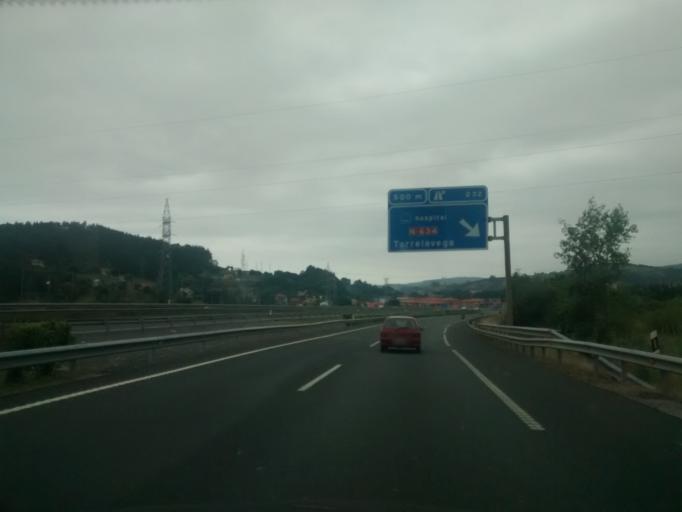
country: ES
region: Cantabria
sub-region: Provincia de Cantabria
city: Reocin
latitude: 43.3557
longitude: -4.0773
